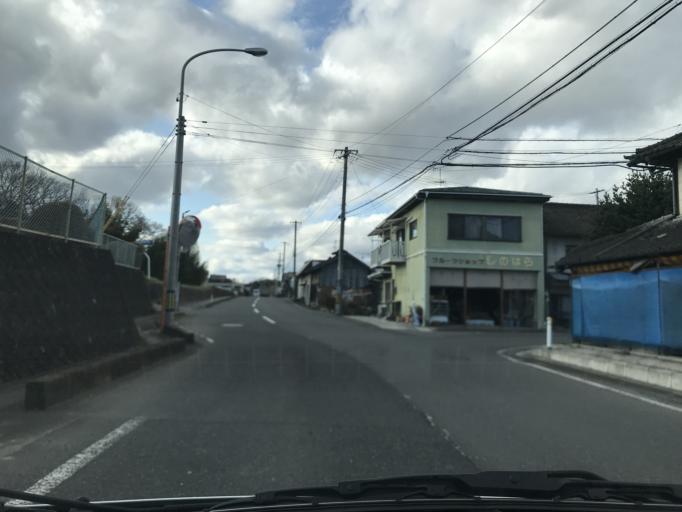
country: JP
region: Miyagi
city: Wakuya
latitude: 38.6284
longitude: 141.2137
